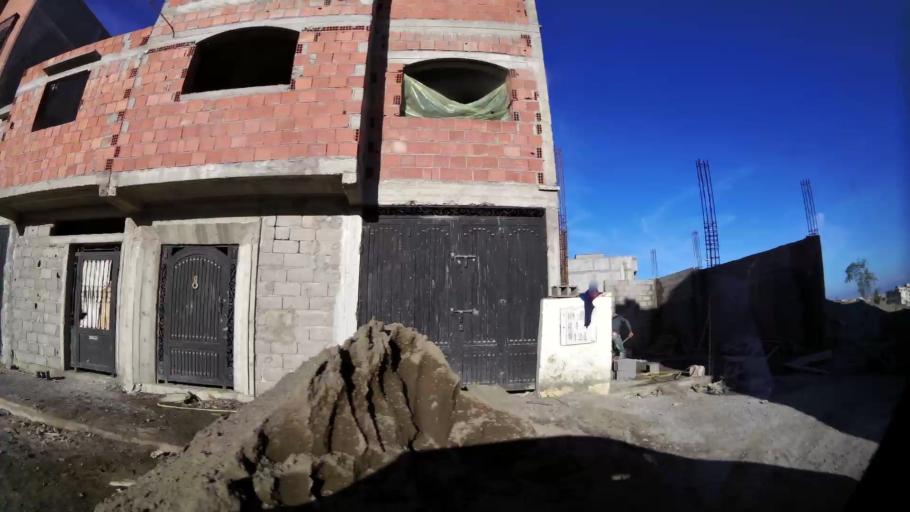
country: MA
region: Marrakech-Tensift-Al Haouz
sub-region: Marrakech
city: Marrakesh
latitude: 31.7675
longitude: -8.1063
